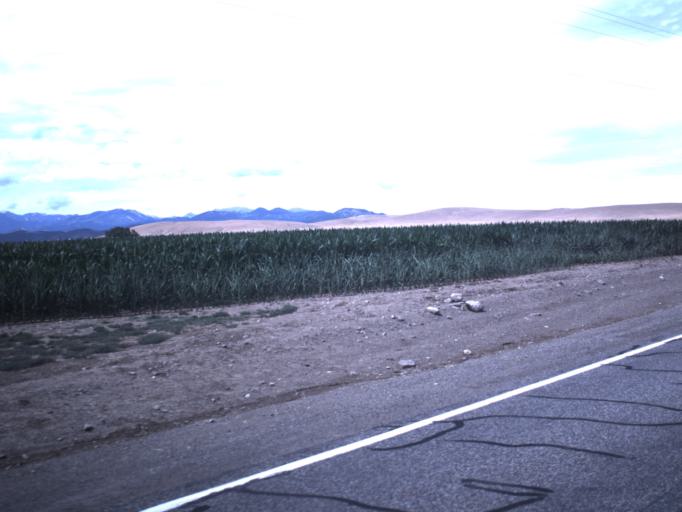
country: US
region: Utah
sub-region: Sevier County
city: Monroe
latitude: 38.6290
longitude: -112.1536
